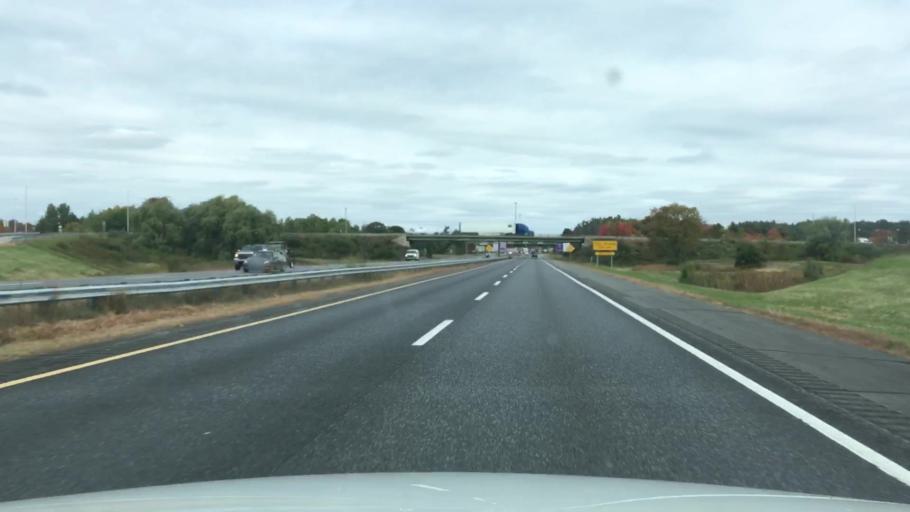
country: US
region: Maine
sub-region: Kennebec County
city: Gardiner
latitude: 44.2071
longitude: -69.8248
